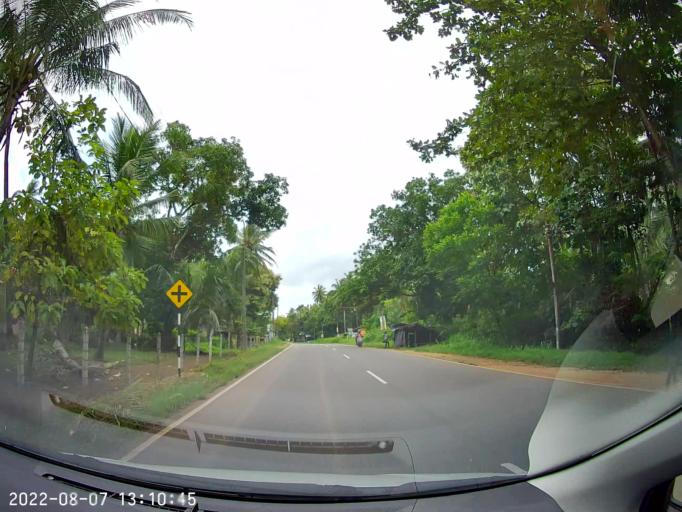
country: LK
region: North Western
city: Kuliyapitiya
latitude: 7.4354
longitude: 80.0299
